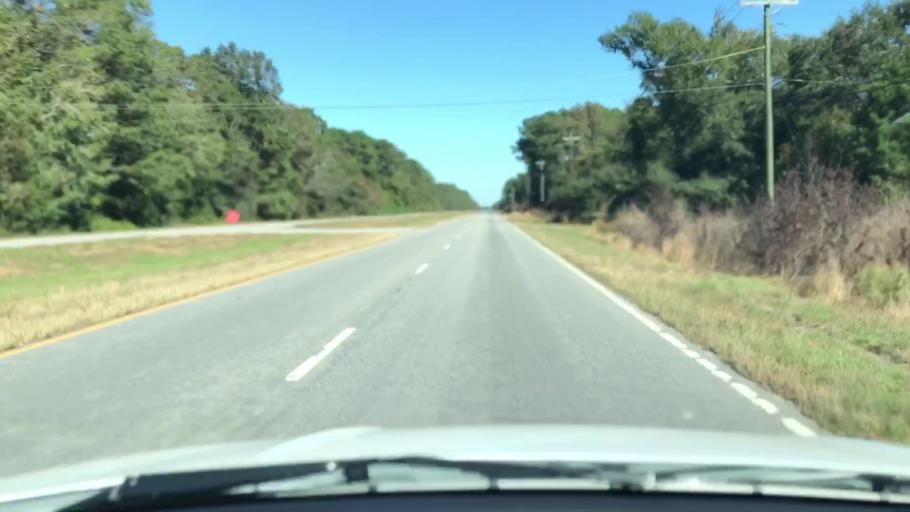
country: US
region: South Carolina
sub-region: Charleston County
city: Ravenel
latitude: 32.7576
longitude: -80.3209
